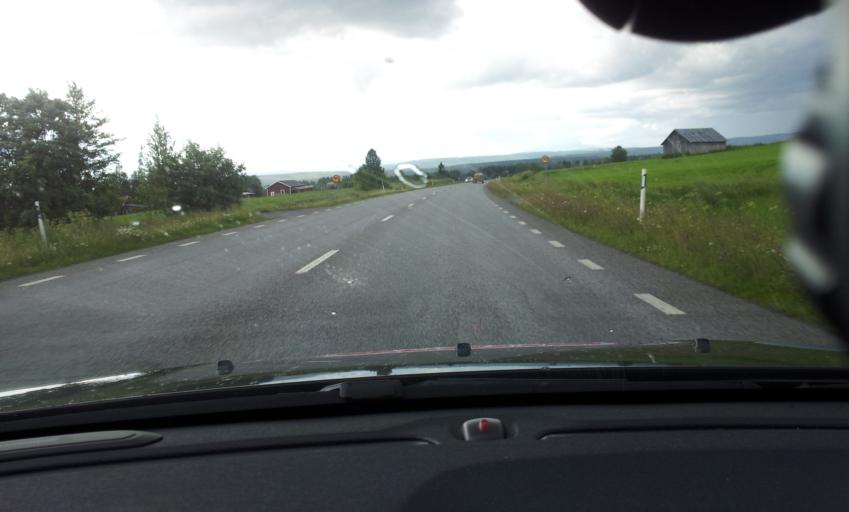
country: SE
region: Jaemtland
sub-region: Krokoms Kommun
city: Valla
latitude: 63.3042
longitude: 13.8868
